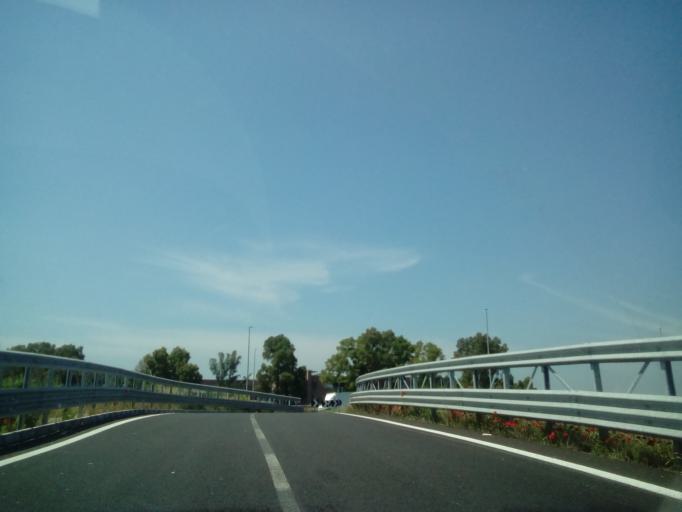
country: IT
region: Latium
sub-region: Citta metropolitana di Roma Capitale
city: Setteville
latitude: 41.8831
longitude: 12.6108
